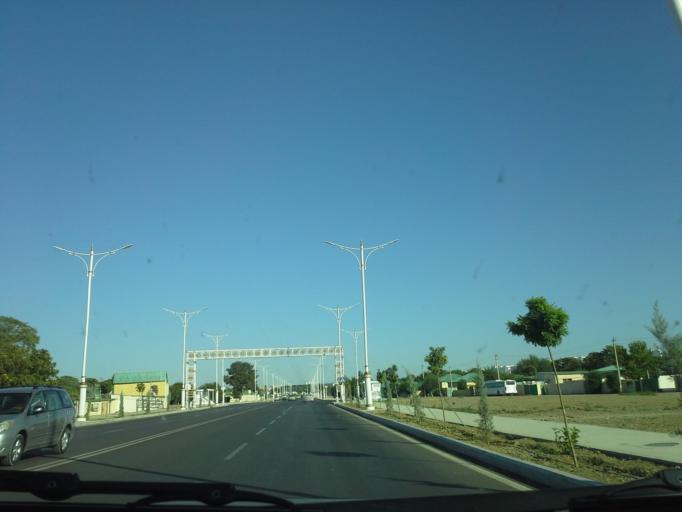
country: TM
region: Ahal
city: Ashgabat
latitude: 37.9627
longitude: 58.3324
